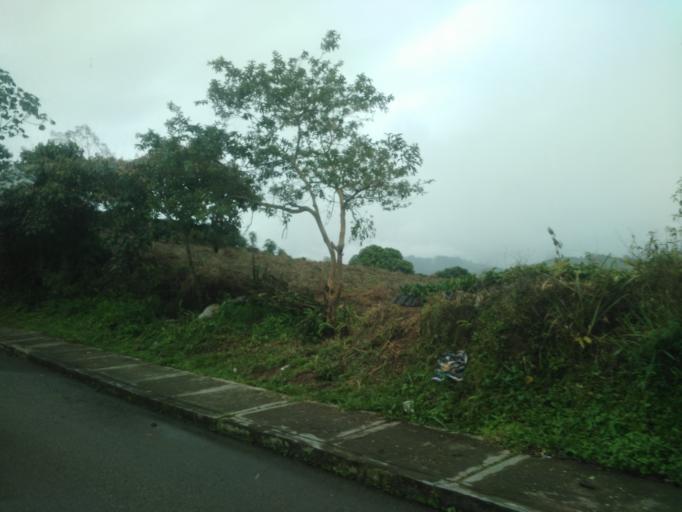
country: CO
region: Valle del Cauca
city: Sevilla
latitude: 4.2689
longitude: -75.9221
